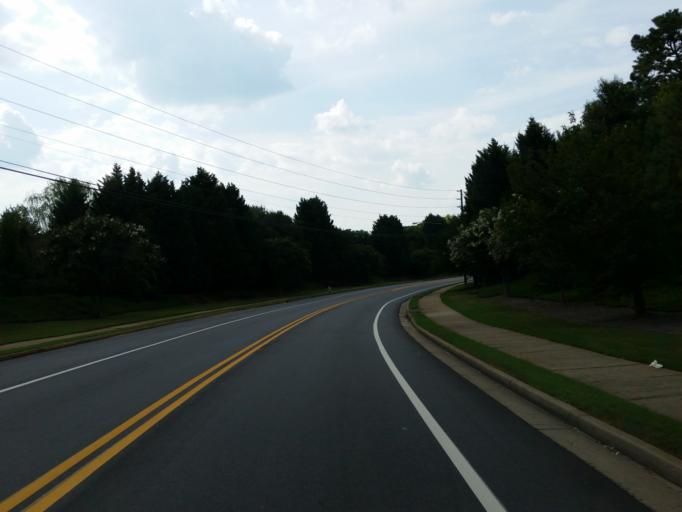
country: US
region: Georgia
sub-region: Fulton County
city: Roswell
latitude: 34.0512
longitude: -84.3814
